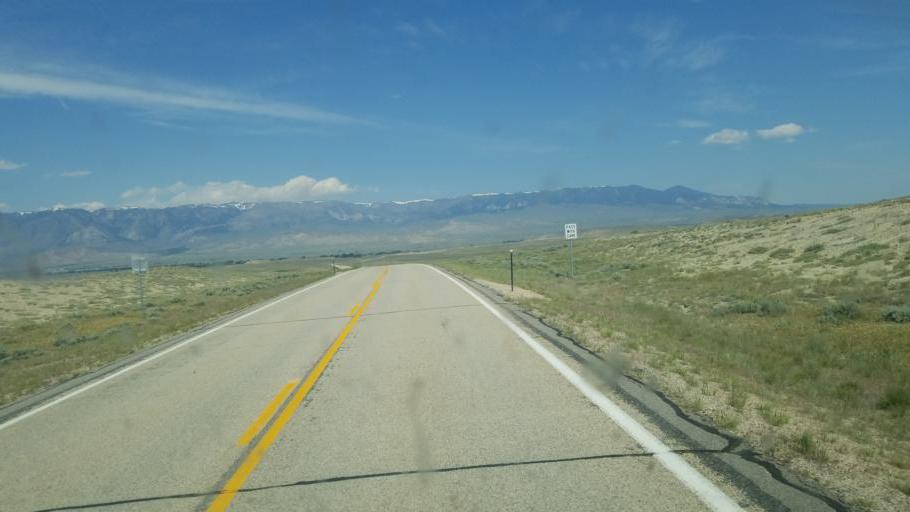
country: US
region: Wyoming
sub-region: Park County
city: Powell
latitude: 44.8854
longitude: -109.0696
